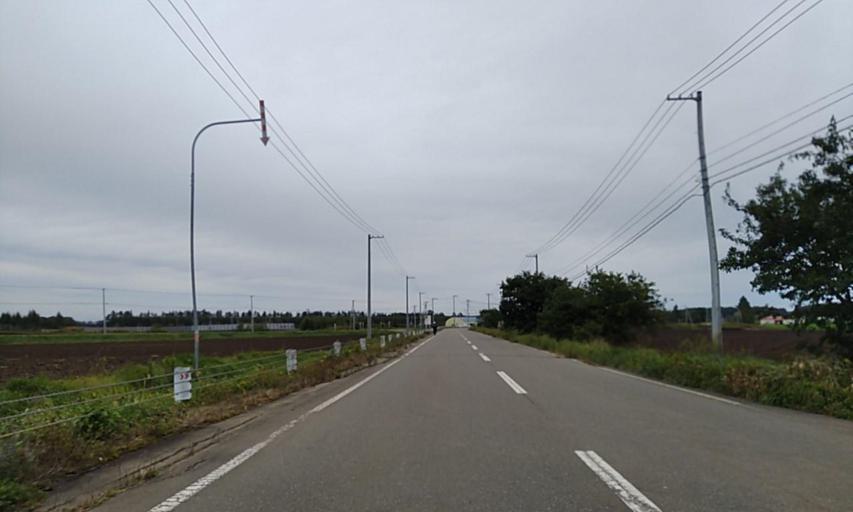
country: JP
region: Hokkaido
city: Obihiro
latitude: 42.6242
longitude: 143.2616
